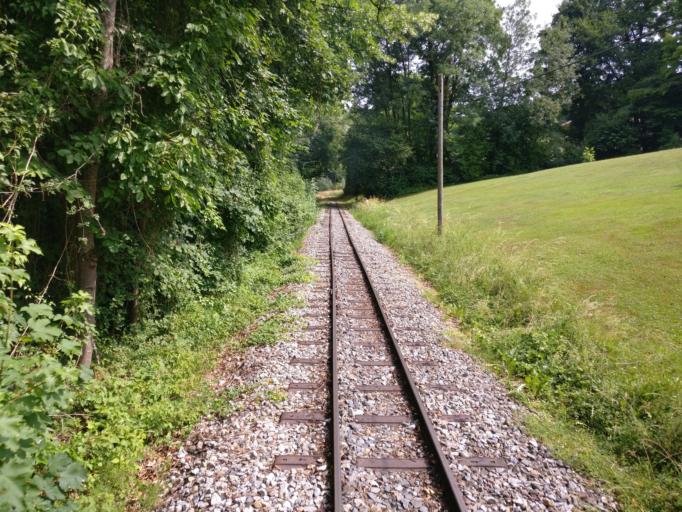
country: AT
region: Upper Austria
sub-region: Politischer Bezirk Steyr-Land
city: Sierning
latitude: 48.0289
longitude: 14.3363
